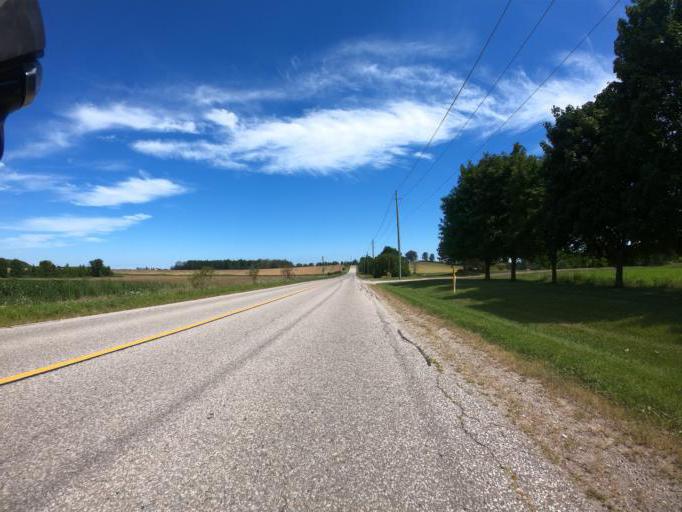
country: CA
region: Ontario
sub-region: Wellington County
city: Guelph
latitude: 43.5398
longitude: -80.3837
